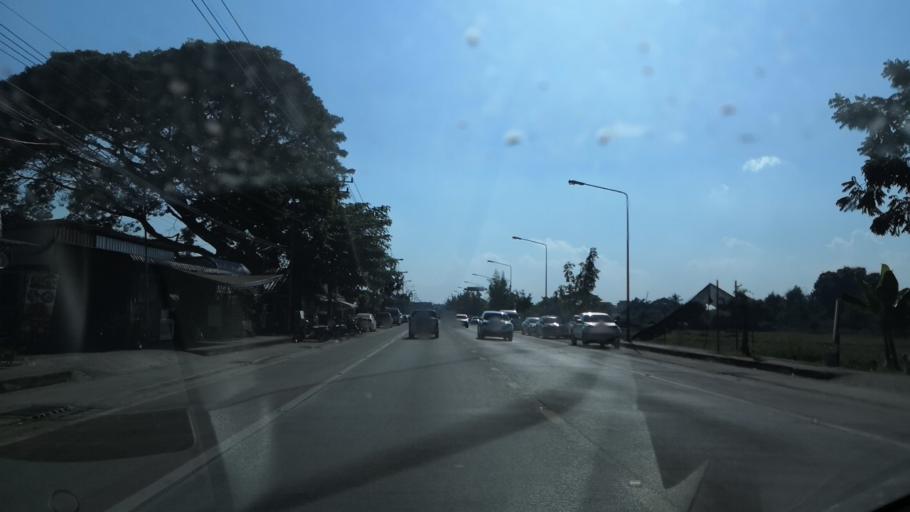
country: TH
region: Chiang Rai
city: Chiang Rai
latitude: 19.9325
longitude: 99.8405
